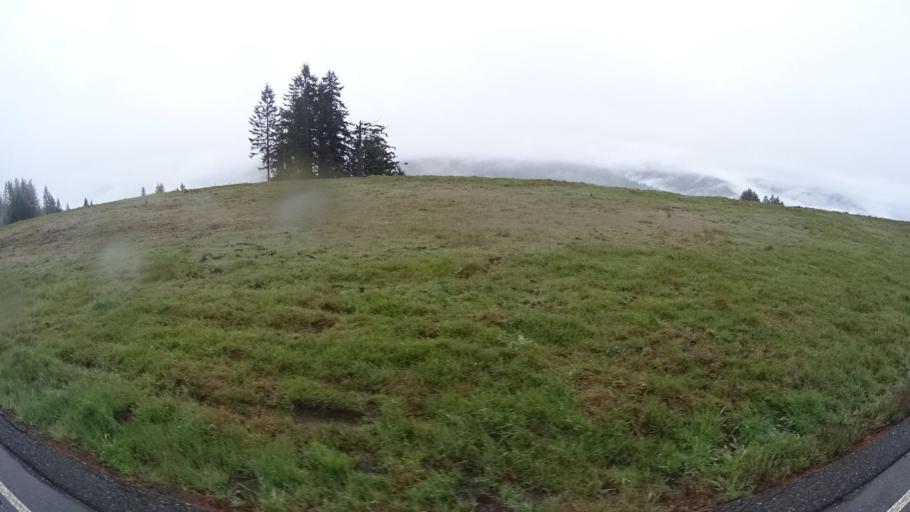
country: US
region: California
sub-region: Humboldt County
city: Westhaven-Moonstone
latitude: 41.1937
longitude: -123.9394
